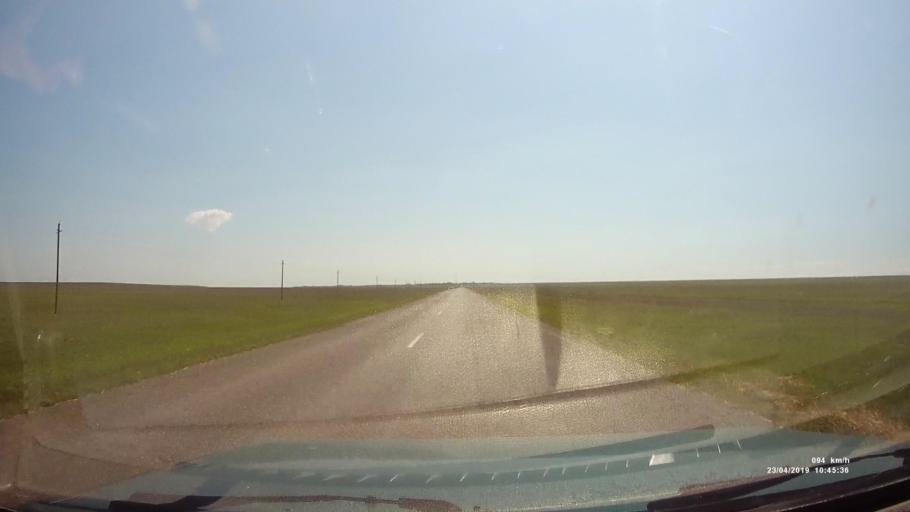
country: RU
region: Kalmykiya
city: Yashalta
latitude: 46.4500
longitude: 42.6771
